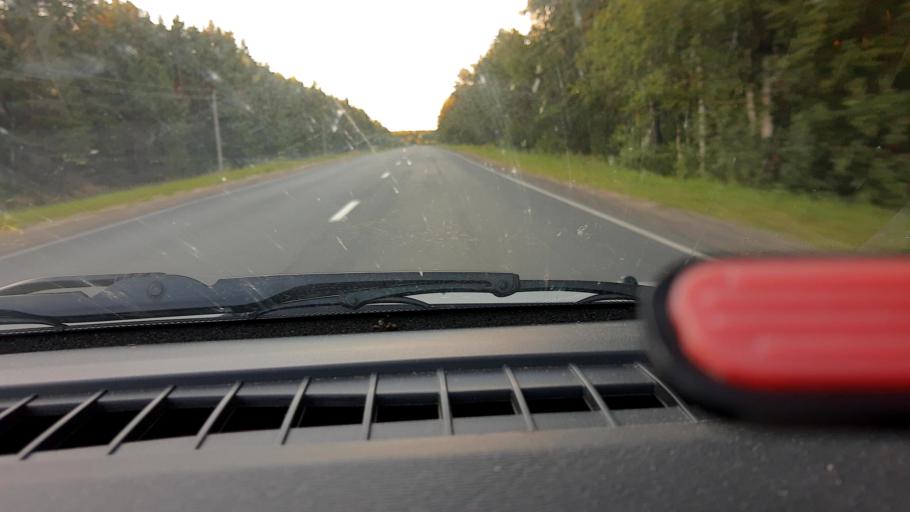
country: RU
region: Nizjnij Novgorod
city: Uren'
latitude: 57.4208
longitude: 45.6881
